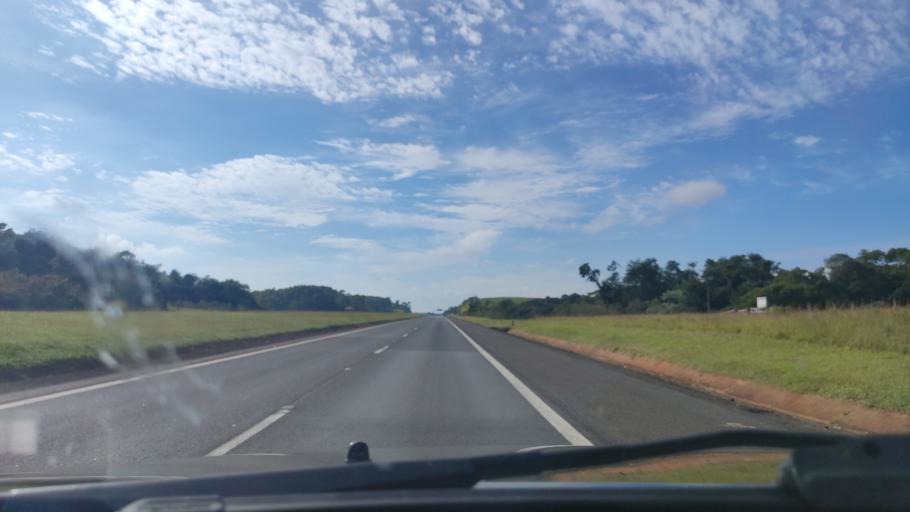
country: BR
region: Sao Paulo
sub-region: Itatinga
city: Itatinga
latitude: -23.0671
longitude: -48.5523
